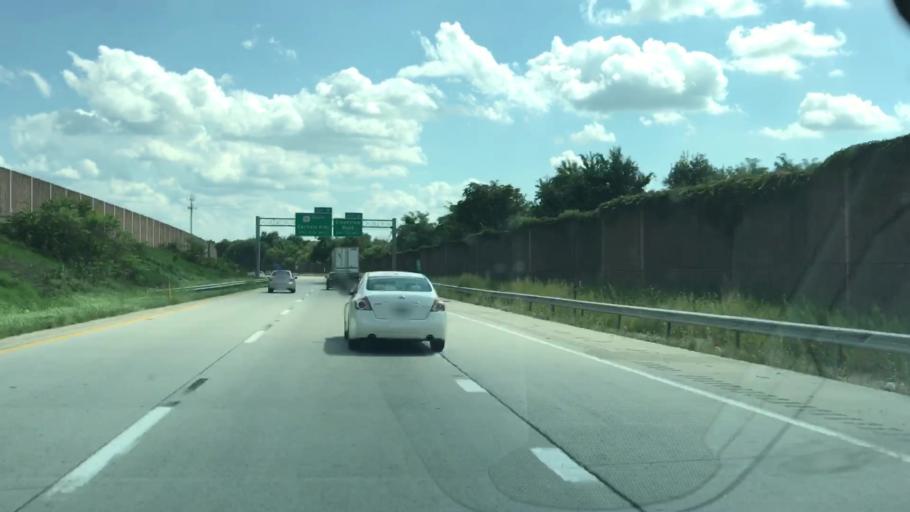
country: US
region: Pennsylvania
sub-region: Cumberland County
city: Mechanicsburg
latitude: 40.2677
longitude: -76.9999
